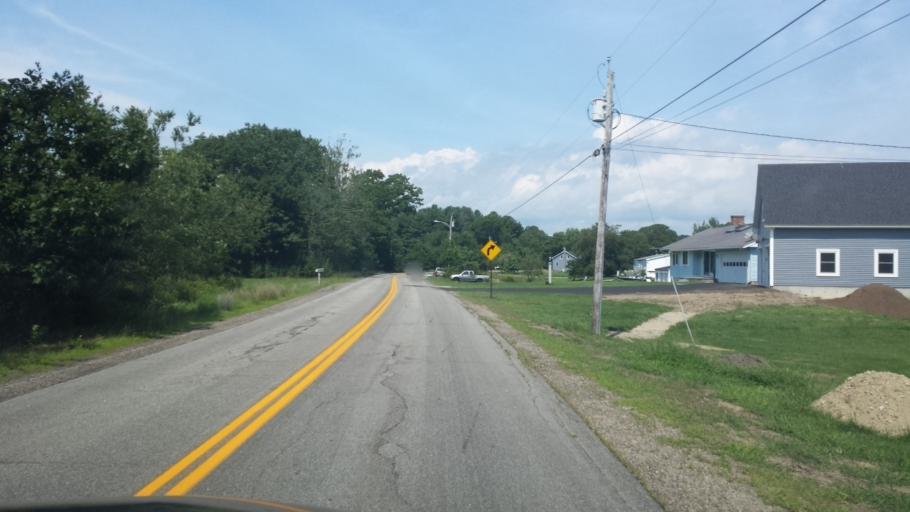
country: US
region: Maine
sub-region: York County
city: Biddeford
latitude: 43.4337
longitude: -70.4060
